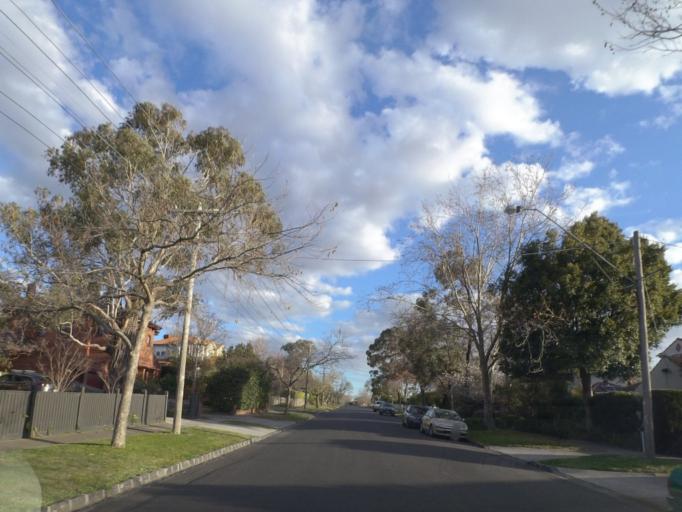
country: AU
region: Victoria
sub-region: Whitehorse
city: Surrey Hills
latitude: -37.8329
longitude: 145.0960
